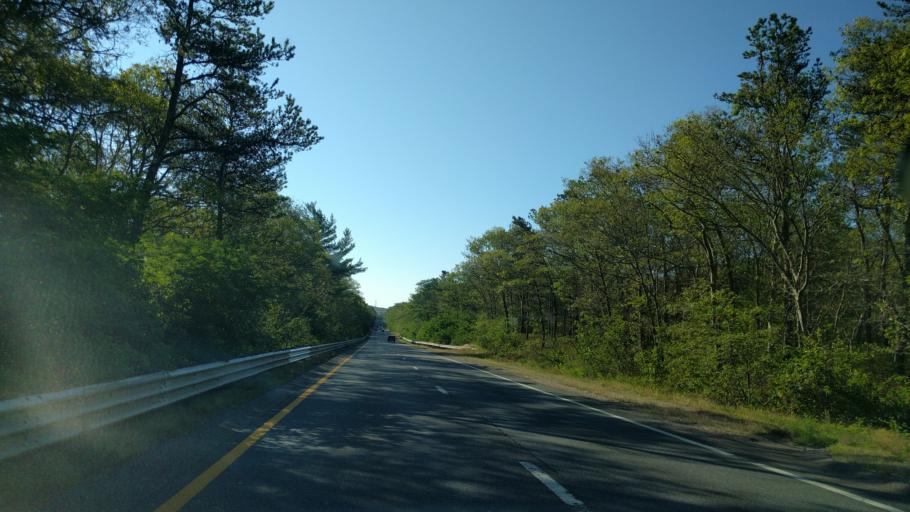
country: US
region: Massachusetts
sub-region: Barnstable County
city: West Barnstable
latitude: 41.7021
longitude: -70.3962
